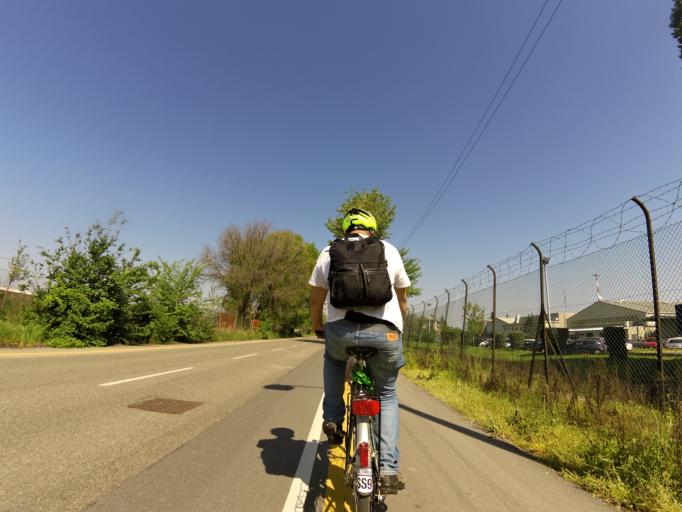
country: IT
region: Lombardy
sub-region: Citta metropolitana di Milano
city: Linate
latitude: 45.4532
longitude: 9.2607
